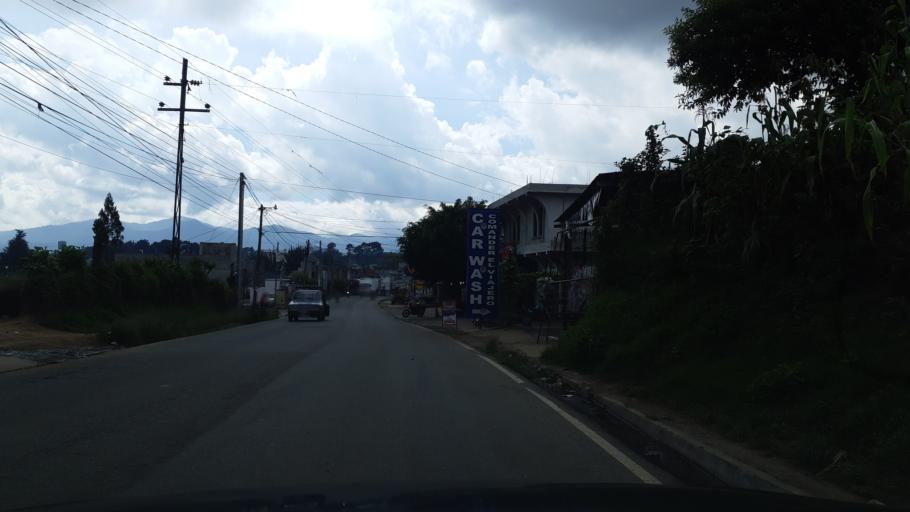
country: GT
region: Chimaltenango
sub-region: Municipio de Chimaltenango
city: Chimaltenango
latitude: 14.6729
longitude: -90.8055
